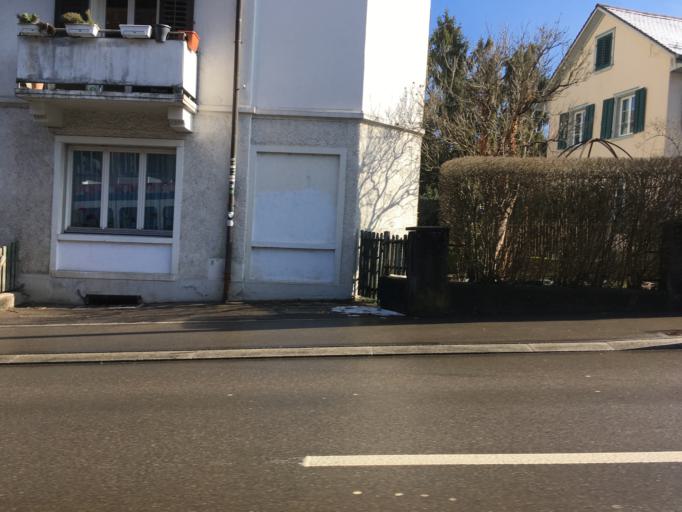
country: CH
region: Zurich
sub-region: Bezirk Zuerich
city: Zuerich (Kreis 8) / Weinegg
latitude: 47.3563
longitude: 8.5736
